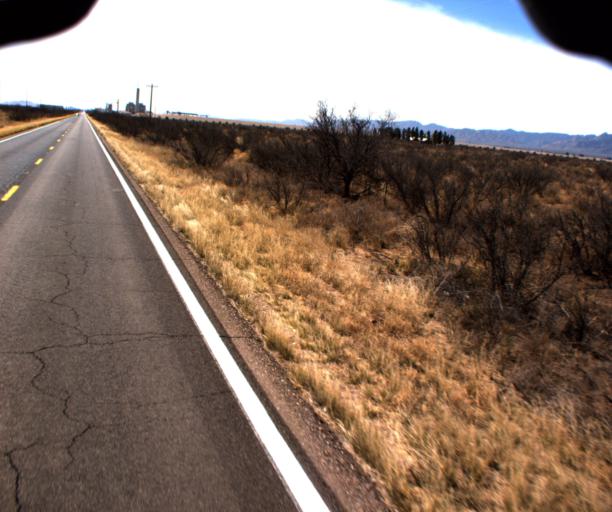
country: US
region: Arizona
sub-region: Cochise County
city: Willcox
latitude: 32.0867
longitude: -109.9045
